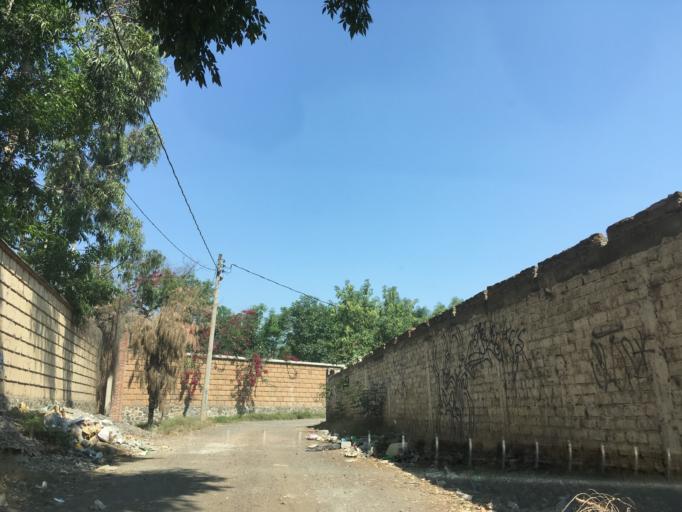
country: MX
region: Michoacan
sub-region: Morelia
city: Morelos
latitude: 19.6704
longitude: -101.2232
